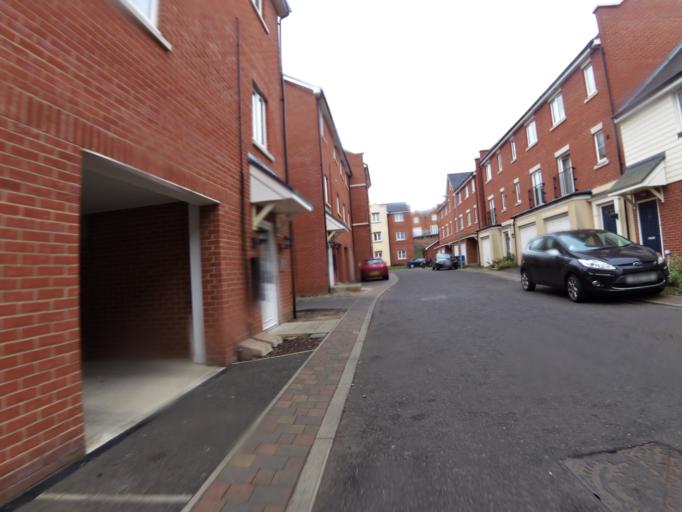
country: GB
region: England
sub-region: Suffolk
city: Ipswich
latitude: 52.0625
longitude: 1.1706
